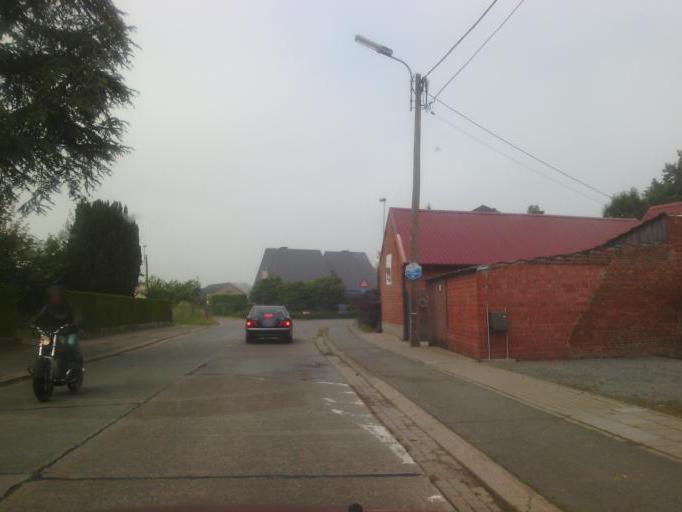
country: BE
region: Flanders
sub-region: Provincie Oost-Vlaanderen
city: Berlare
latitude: 50.9962
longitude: 4.0237
